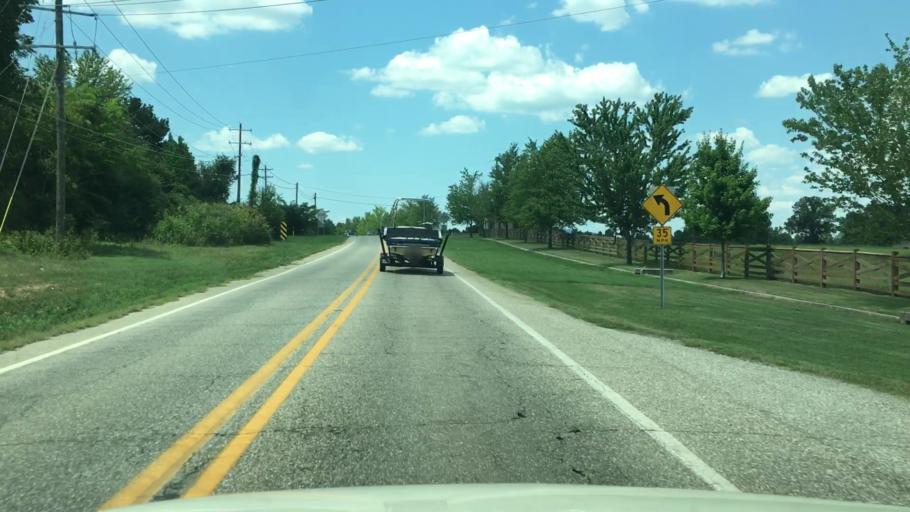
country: US
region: Arkansas
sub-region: Garland County
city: Lake Hamilton
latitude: 34.4060
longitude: -93.0908
